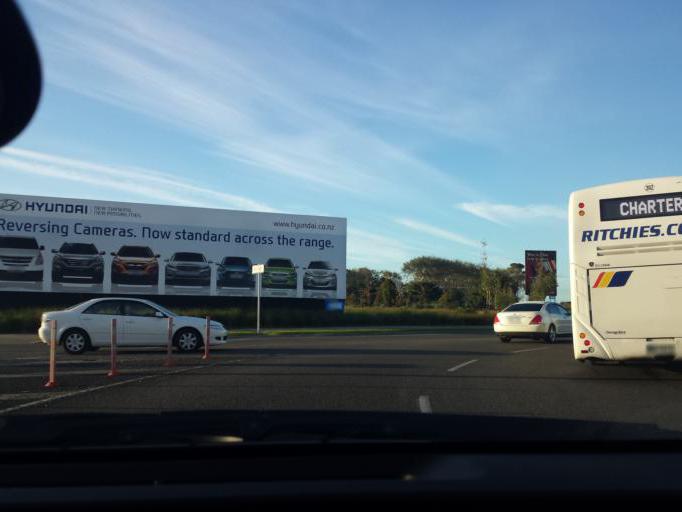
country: NZ
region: Auckland
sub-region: Auckland
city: Mangere
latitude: -36.9909
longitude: 174.7864
